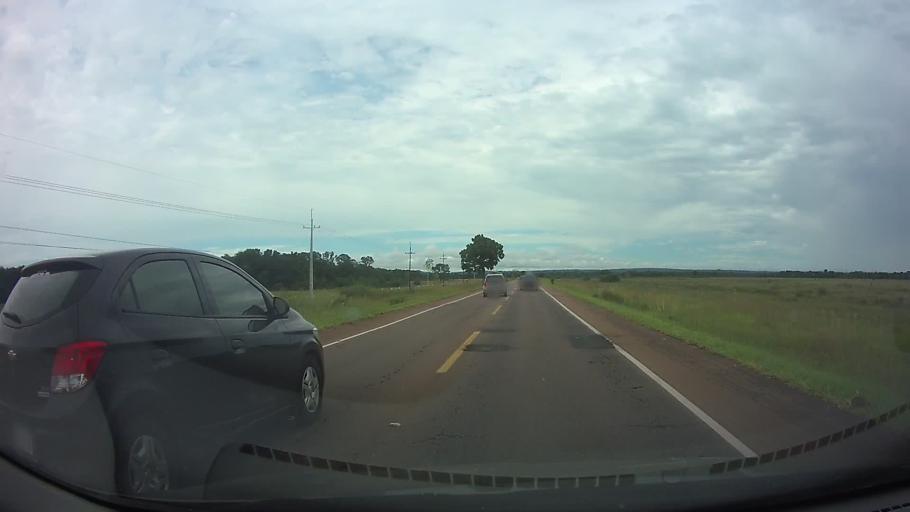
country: PY
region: Paraguari
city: Carapegua
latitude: -25.7156
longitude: -57.1952
